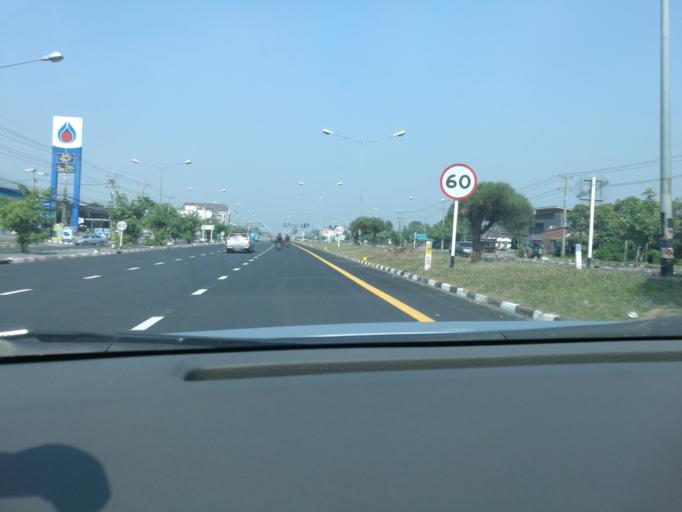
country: TH
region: Sara Buri
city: Saraburi
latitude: 14.5514
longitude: 100.9074
